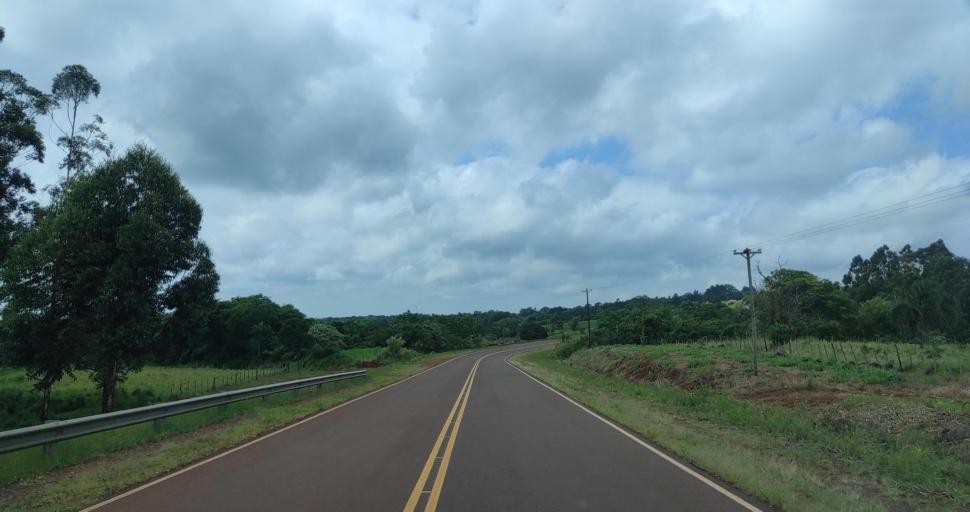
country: AR
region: Misiones
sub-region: Departamento de Veinticinco de Mayo
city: Veinticinco de Mayo
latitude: -27.3515
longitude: -54.8732
